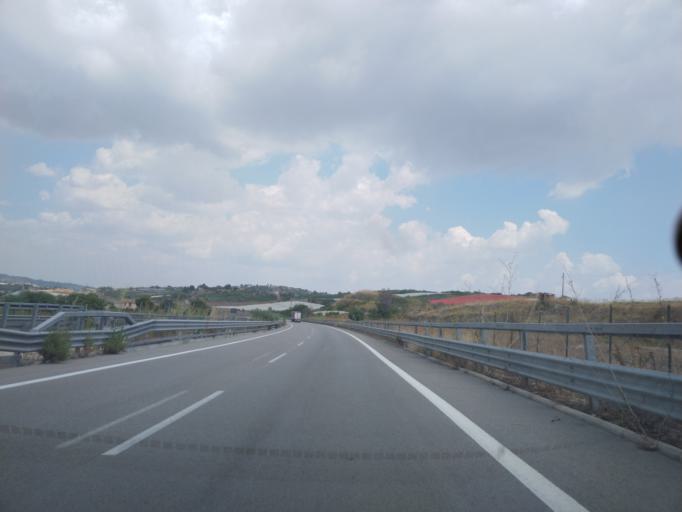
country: IT
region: Sicily
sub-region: Agrigento
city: Canicatti
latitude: 37.3833
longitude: 13.8210
